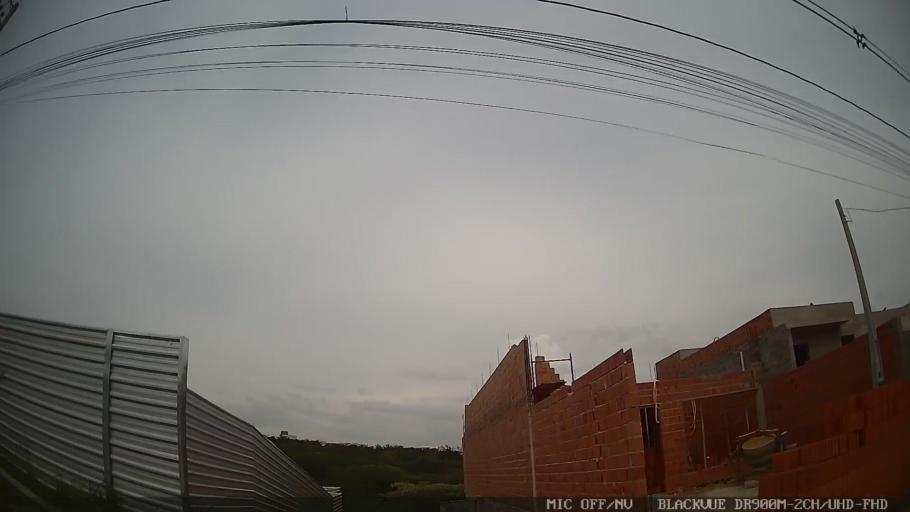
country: BR
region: Sao Paulo
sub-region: Indaiatuba
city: Indaiatuba
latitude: -23.0907
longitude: -47.2469
